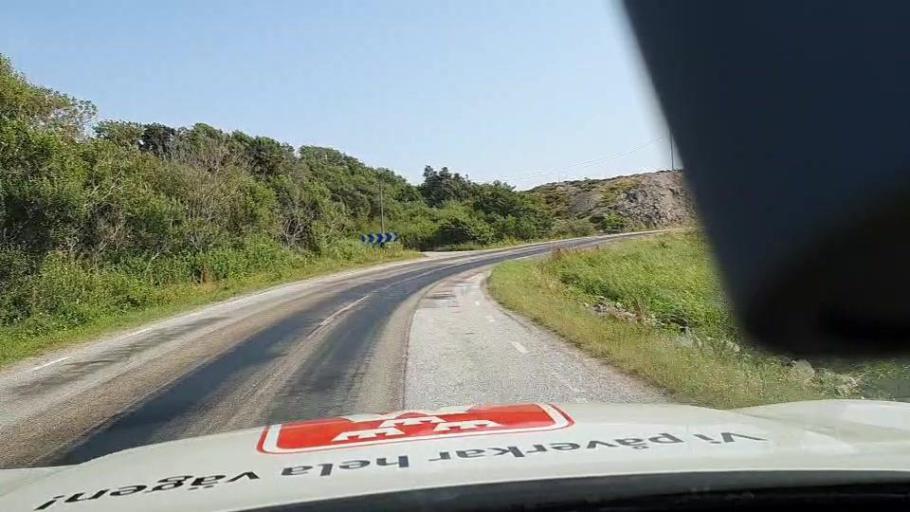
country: SE
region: Vaestra Goetaland
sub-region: Tjorns Kommun
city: Skaerhamn
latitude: 58.0966
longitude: 11.4907
